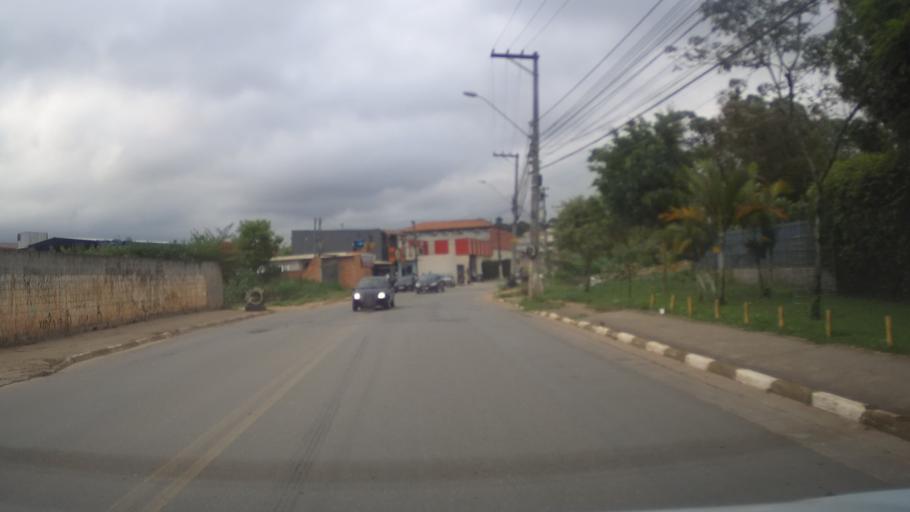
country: BR
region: Sao Paulo
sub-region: Aruja
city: Aruja
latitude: -23.4148
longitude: -46.3849
